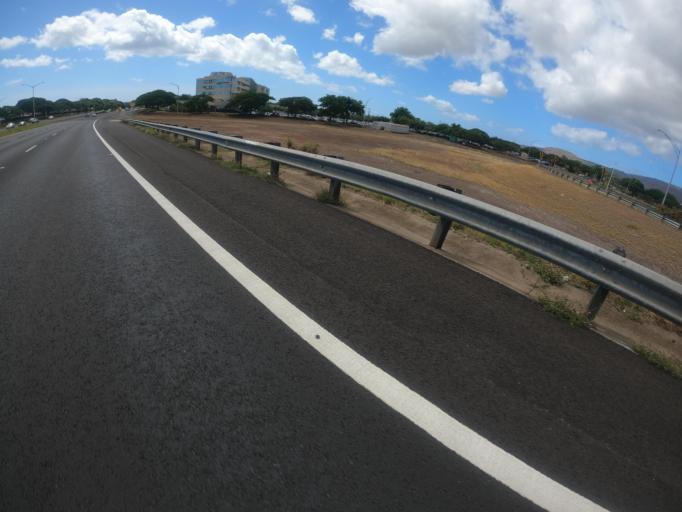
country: US
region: Hawaii
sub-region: Honolulu County
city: Royal Kunia
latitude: 21.3745
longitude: -158.0263
